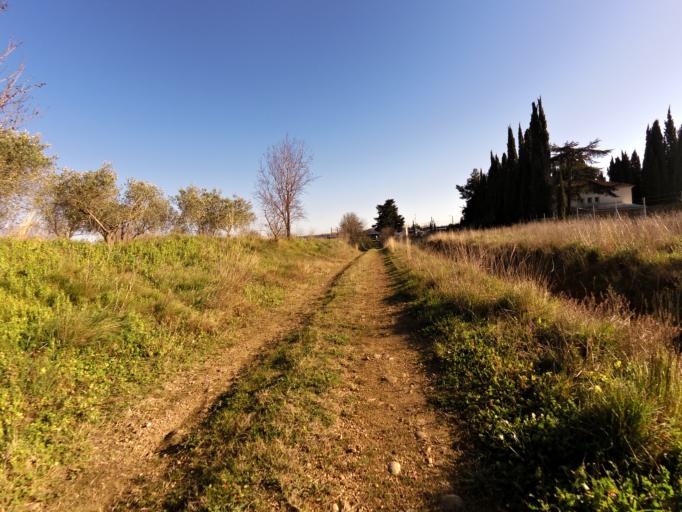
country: FR
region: Languedoc-Roussillon
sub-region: Departement du Gard
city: Mus
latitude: 43.7300
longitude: 4.1956
